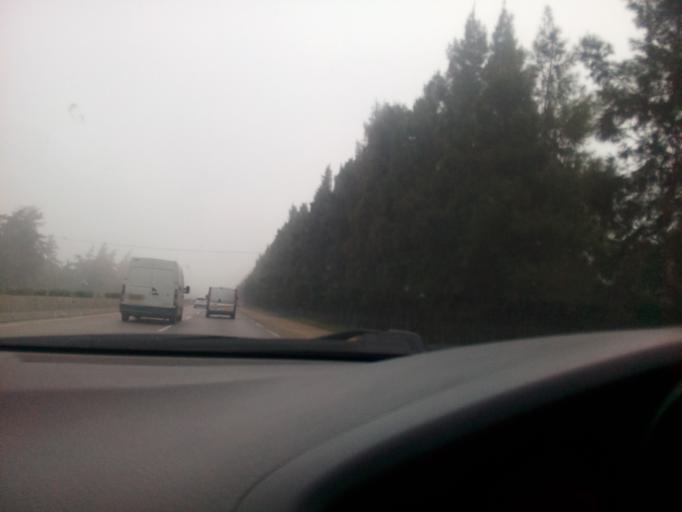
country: DZ
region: Oran
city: Bou Tlelis
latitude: 35.5809
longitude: -0.8314
